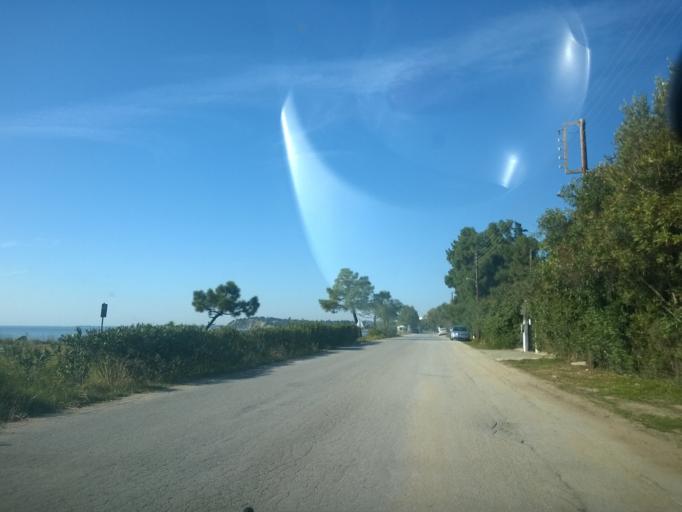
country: GR
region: Central Macedonia
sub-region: Nomos Chalkidikis
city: Nea Kallikrateia
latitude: 40.3393
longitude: 23.0176
